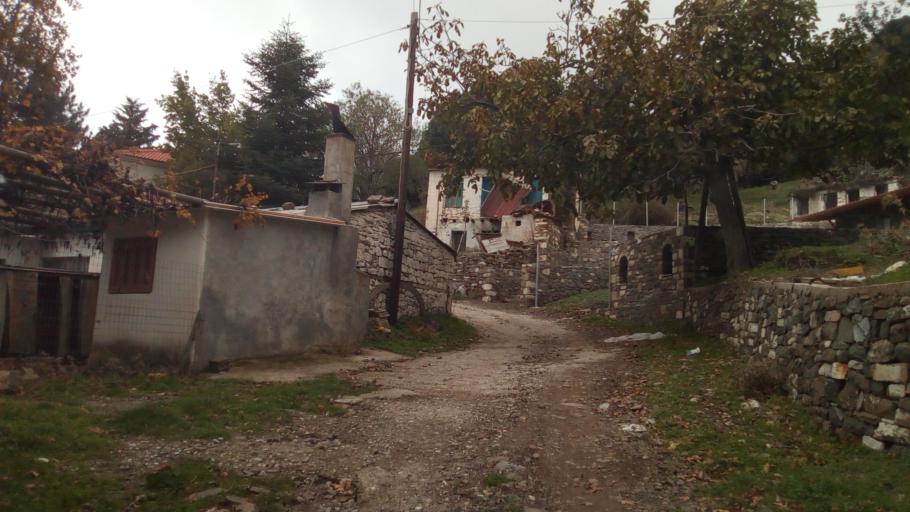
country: GR
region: Central Greece
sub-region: Nomos Fokidos
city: Lidoriki
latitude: 38.4163
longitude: 22.0994
